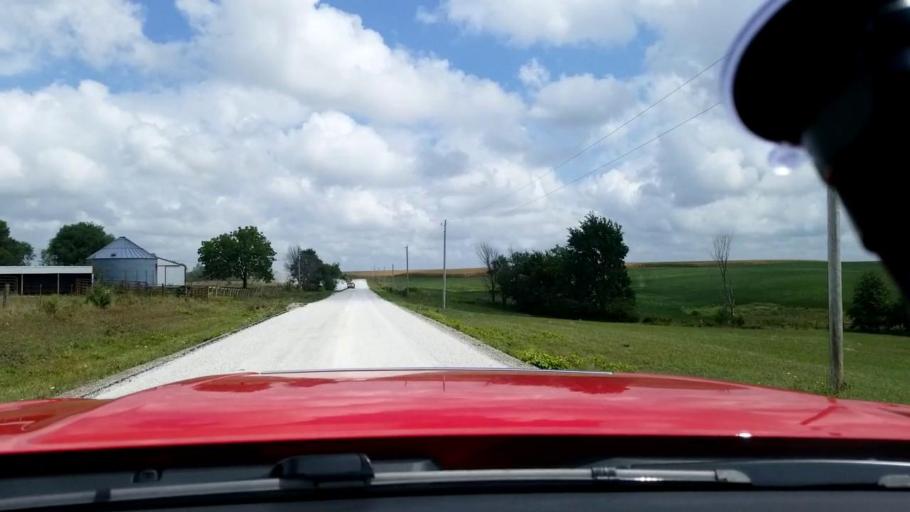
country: US
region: Iowa
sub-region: Decatur County
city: Lamoni
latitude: 40.6544
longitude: -94.0518
